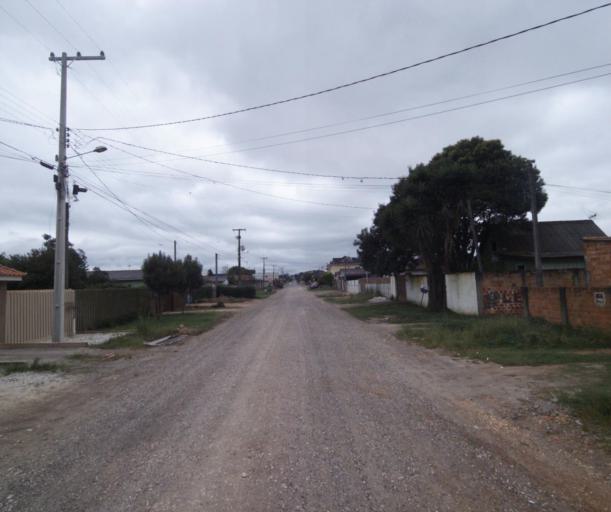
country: BR
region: Parana
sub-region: Quatro Barras
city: Quatro Barras
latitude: -25.3616
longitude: -49.0971
